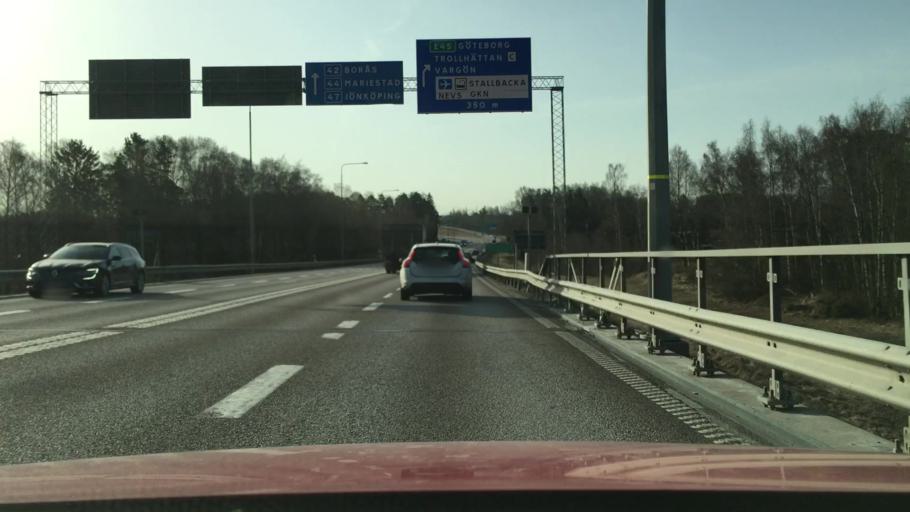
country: SE
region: Vaestra Goetaland
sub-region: Trollhattan
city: Trollhattan
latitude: 58.3047
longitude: 12.3241
